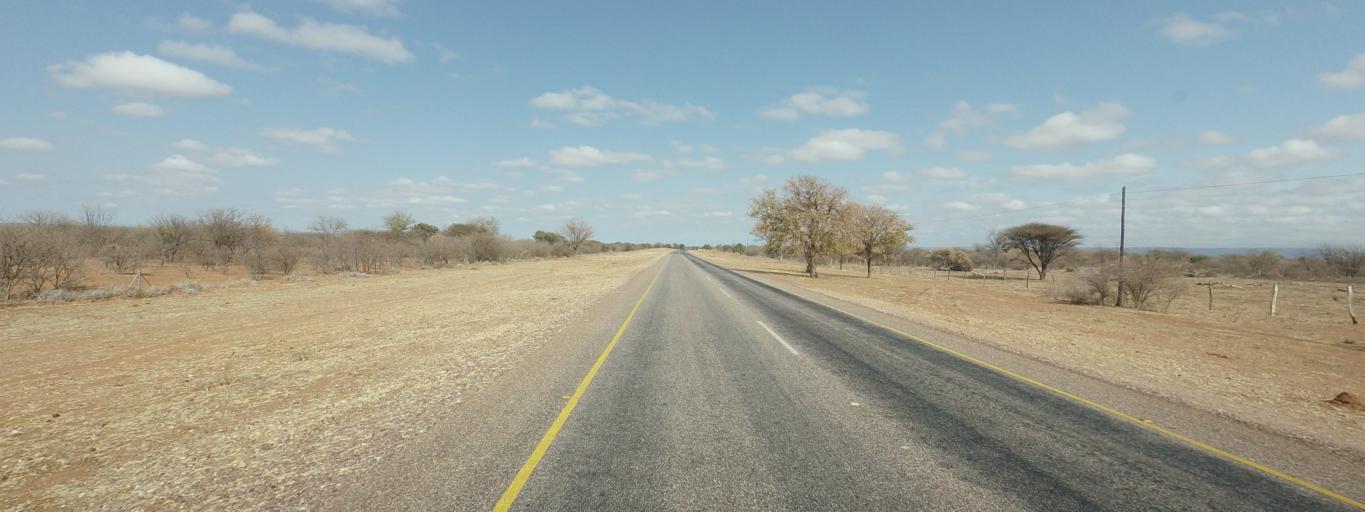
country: BW
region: Central
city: Ratholo
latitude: -22.8155
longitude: 27.5598
